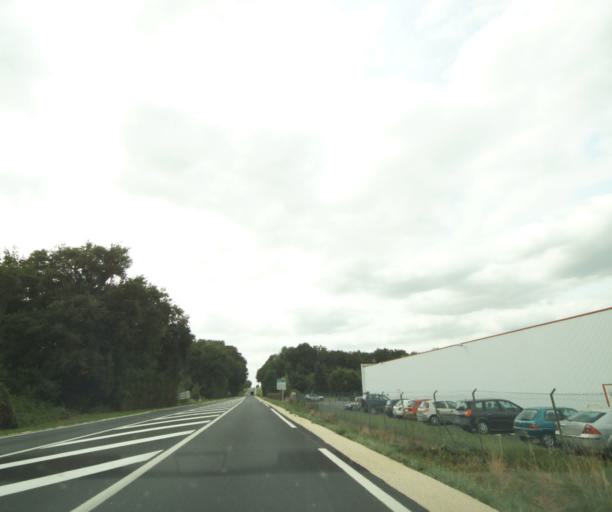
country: FR
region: Centre
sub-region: Departement de l'Indre
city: Buzancais
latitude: 46.8928
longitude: 1.3950
